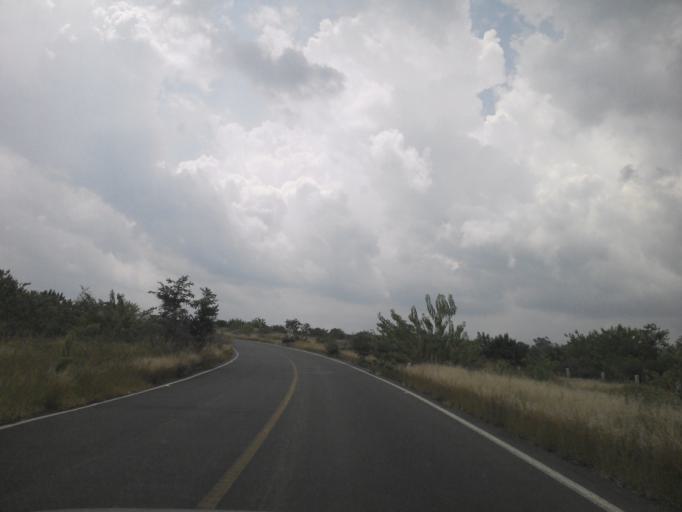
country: MX
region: Jalisco
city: San Diego de Alejandria
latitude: 20.9042
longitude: -101.9848
